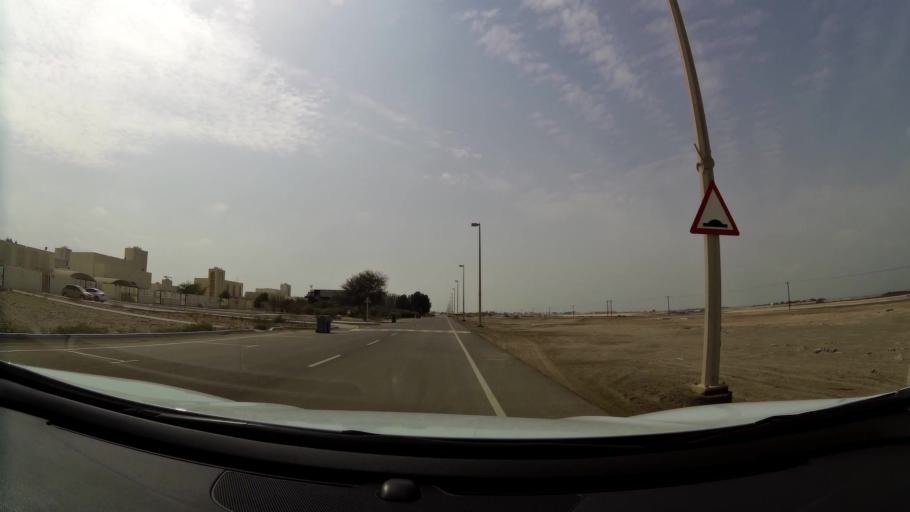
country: AE
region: Abu Dhabi
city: Abu Dhabi
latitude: 24.5650
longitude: 54.6385
